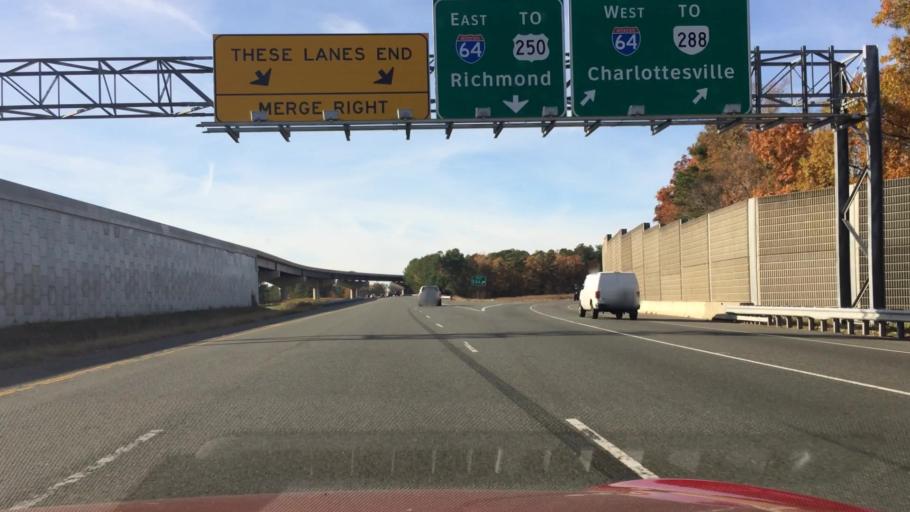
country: US
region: Virginia
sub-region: Henrico County
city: Short Pump
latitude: 37.6594
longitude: -77.6018
